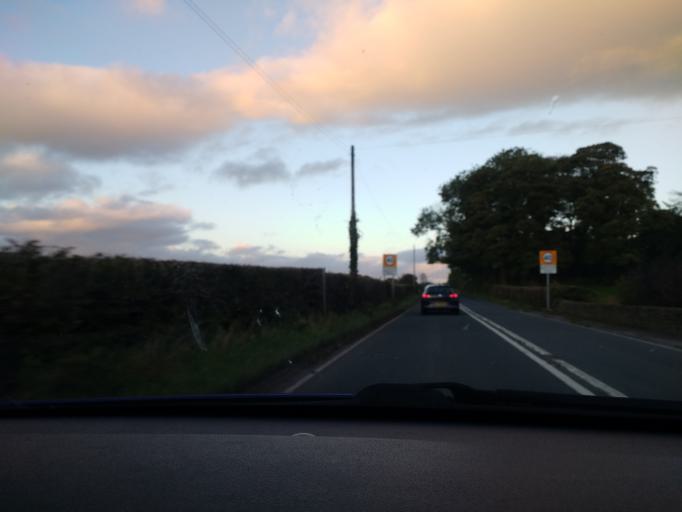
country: GB
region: England
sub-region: Lancashire
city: Caton
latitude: 54.0877
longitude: -2.6791
